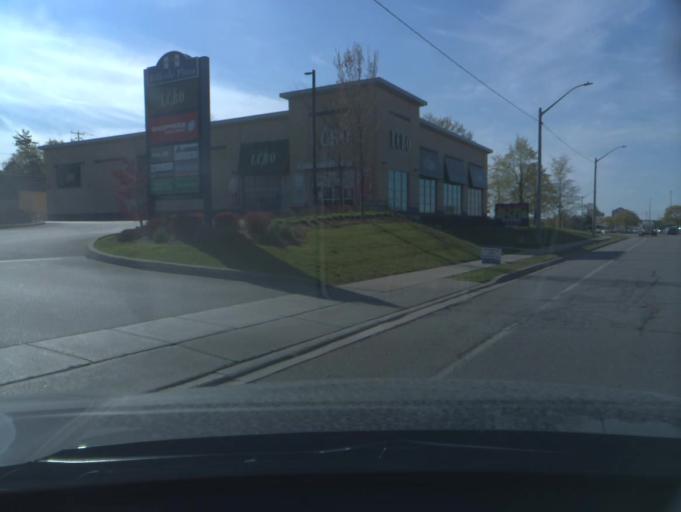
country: CA
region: Ontario
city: North Perth
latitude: 43.8371
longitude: -80.9999
